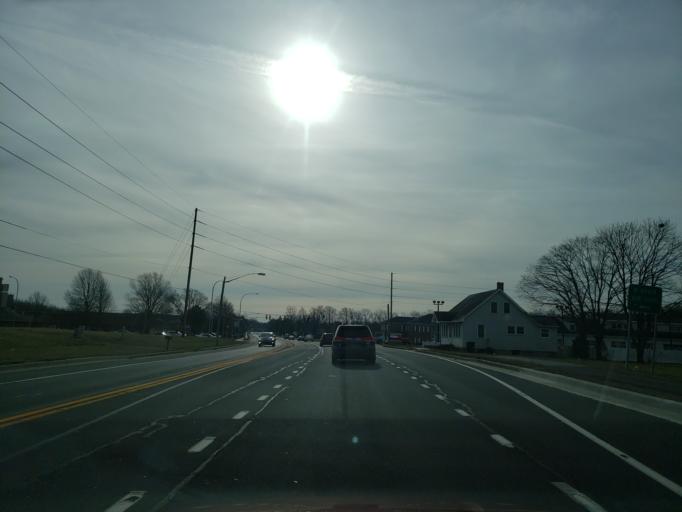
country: US
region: Delaware
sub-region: Kent County
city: Dover
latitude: 39.1770
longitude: -75.5546
